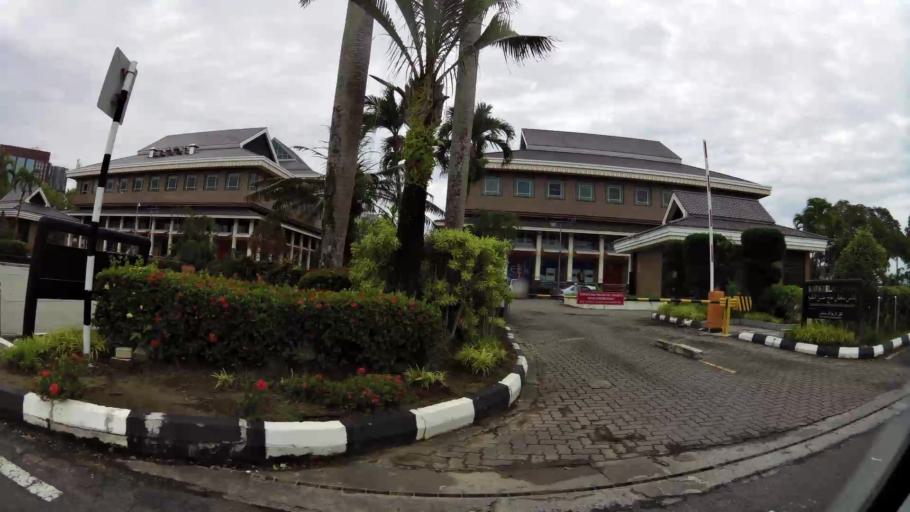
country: BN
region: Brunei and Muara
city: Bandar Seri Begawan
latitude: 4.8884
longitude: 114.9399
